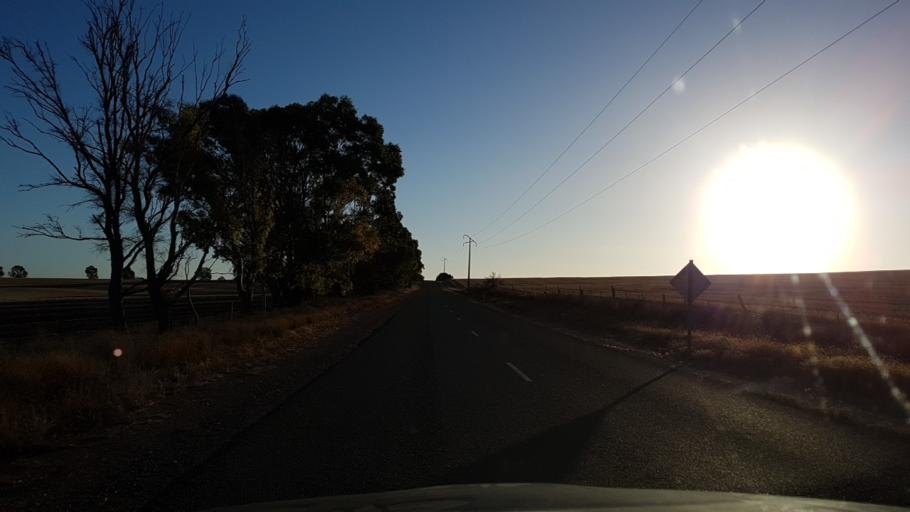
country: AU
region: South Australia
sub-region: Clare and Gilbert Valleys
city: Clare
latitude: -34.0203
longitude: 138.7025
